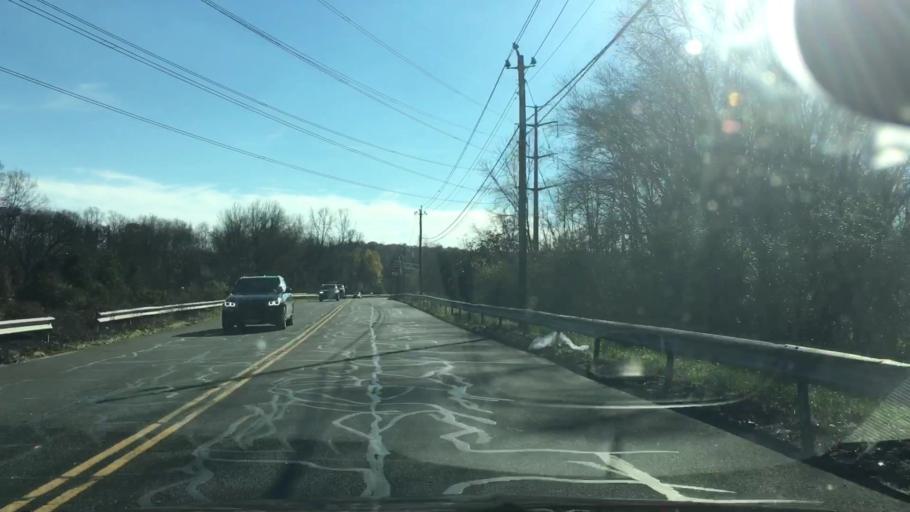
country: US
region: Connecticut
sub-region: Fairfield County
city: Bethel
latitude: 41.4427
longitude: -73.3964
